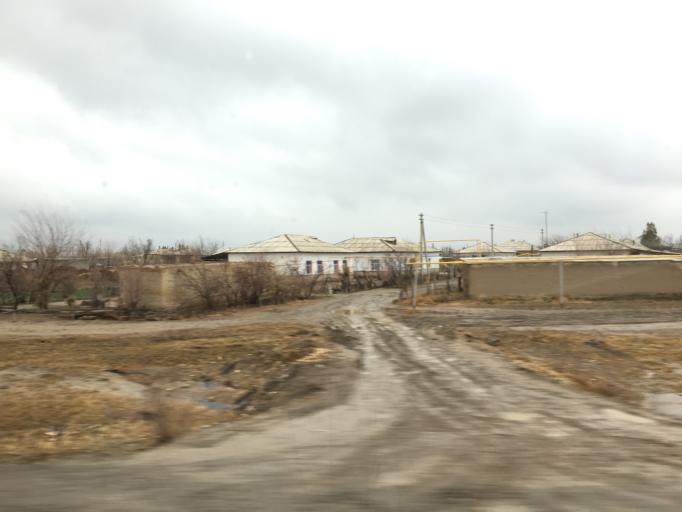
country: TM
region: Mary
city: Yoloeten
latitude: 37.3067
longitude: 62.3229
